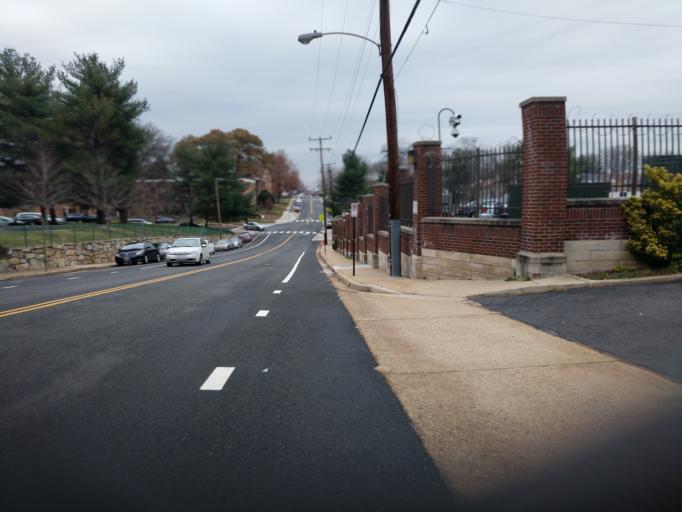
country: US
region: Virginia
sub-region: Arlington County
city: Arlington
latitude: 38.8679
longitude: -77.0811
